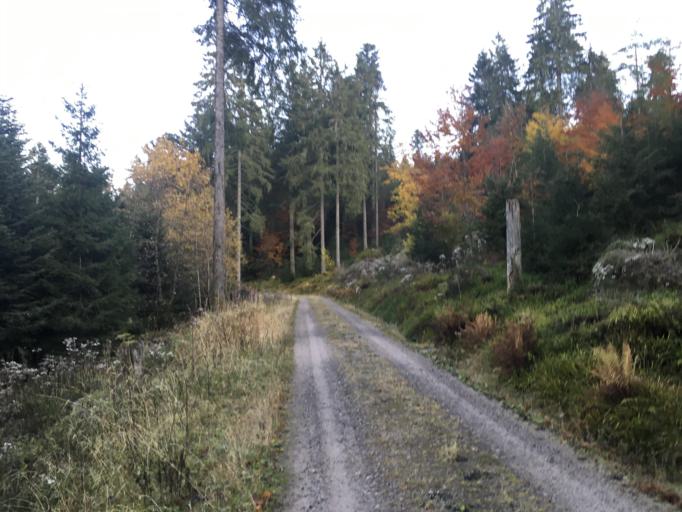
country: DE
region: Baden-Wuerttemberg
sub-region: Freiburg Region
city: Bad Peterstal-Griesbach
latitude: 48.4987
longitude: 8.2579
